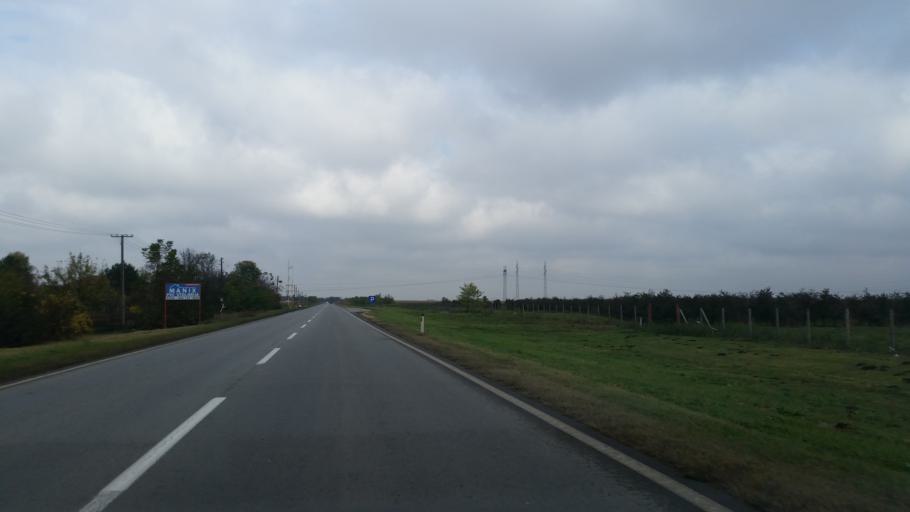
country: RS
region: Autonomna Pokrajina Vojvodina
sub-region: Srednjebanatski Okrug
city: Zrenjanin
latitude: 45.4064
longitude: 20.3752
